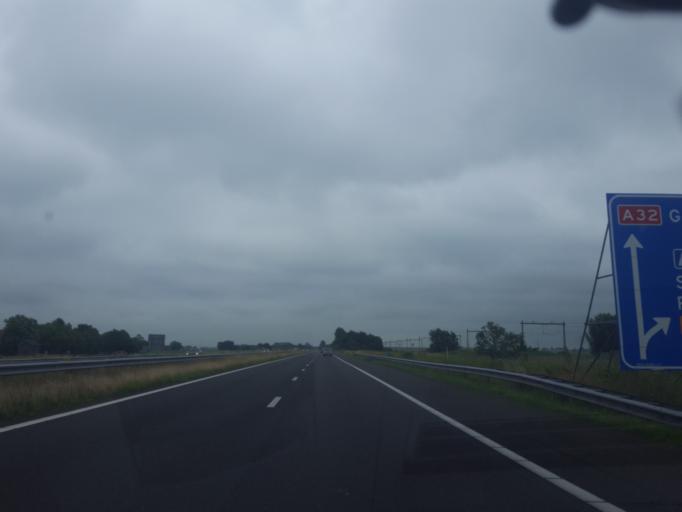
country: NL
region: Friesland
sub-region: Gemeente Boarnsterhim
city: Reduzum
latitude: 53.1248
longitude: 5.8059
